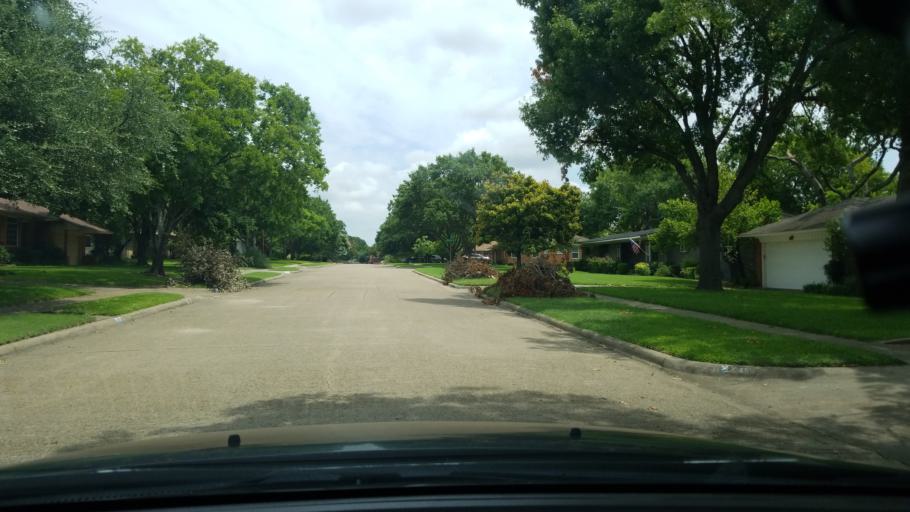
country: US
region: Texas
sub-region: Dallas County
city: Garland
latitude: 32.8270
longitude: -96.6901
